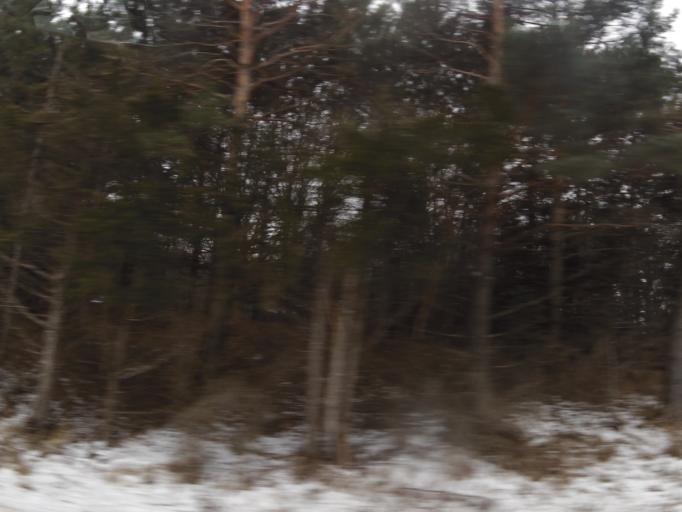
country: US
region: Minnesota
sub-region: Scott County
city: Jordan
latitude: 44.6307
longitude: -93.6084
